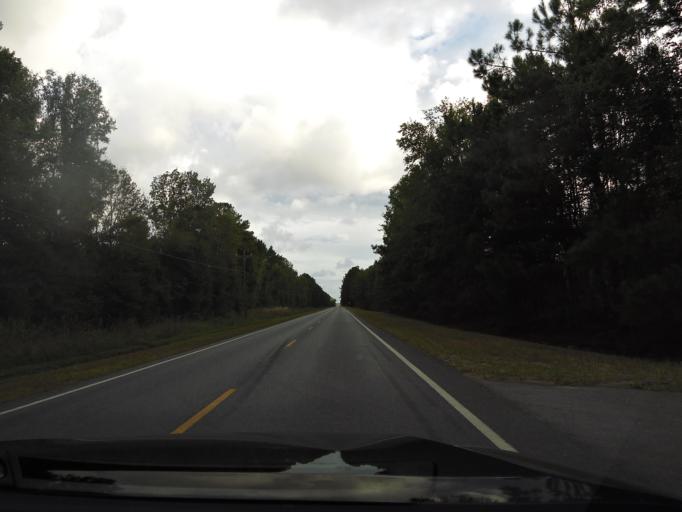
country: US
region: Georgia
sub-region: Liberty County
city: Midway
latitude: 31.6807
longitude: -81.4053
